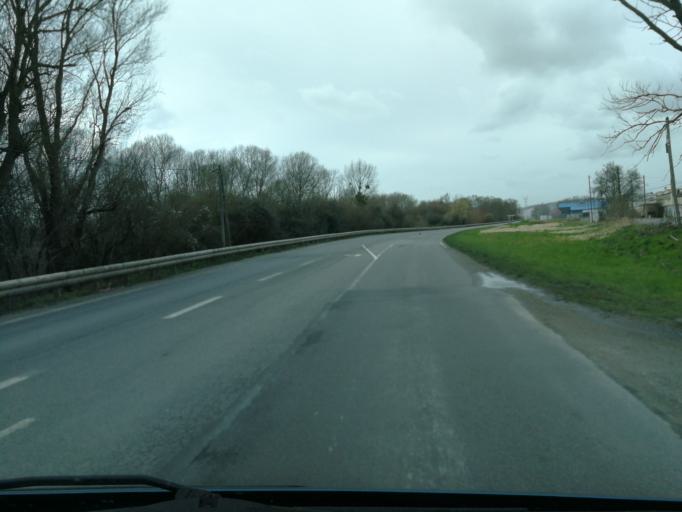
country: FR
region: Haute-Normandie
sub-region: Departement de l'Eure
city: Quillebeuf-sur-Seine
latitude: 49.4851
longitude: 0.5255
